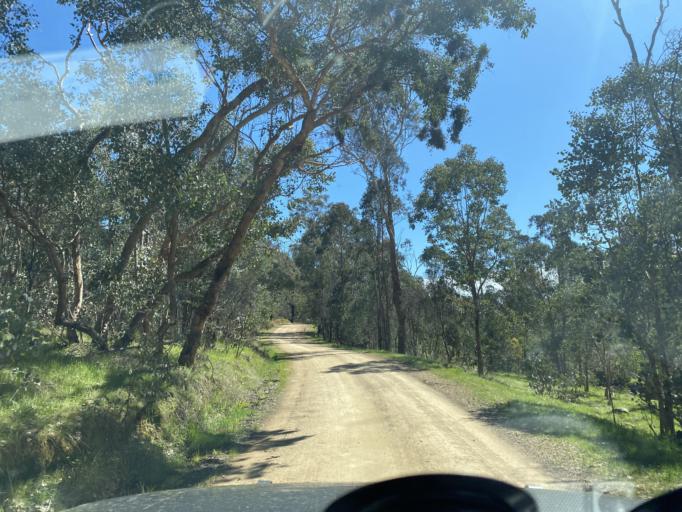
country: AU
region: Victoria
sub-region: Benalla
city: Benalla
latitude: -36.7078
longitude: 146.1784
